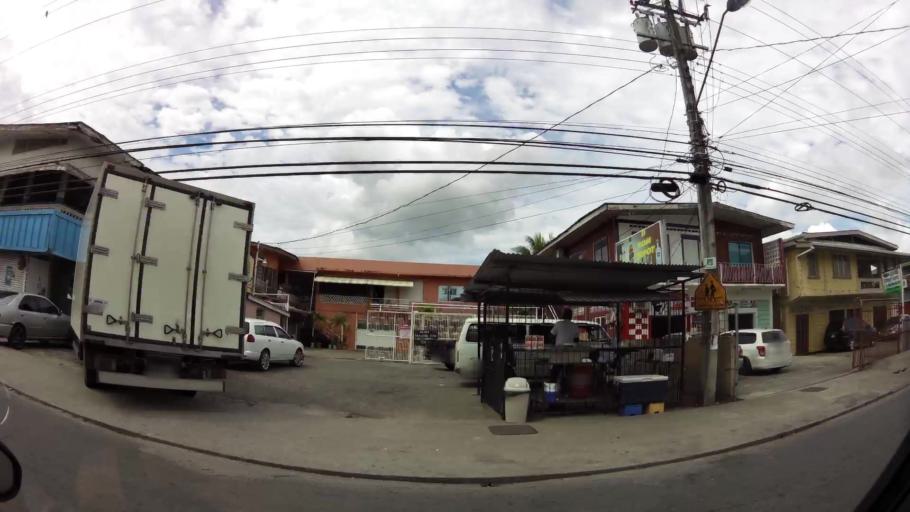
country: TT
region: Couva-Tabaquite-Talparo
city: Couva
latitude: 10.4092
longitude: -61.4715
